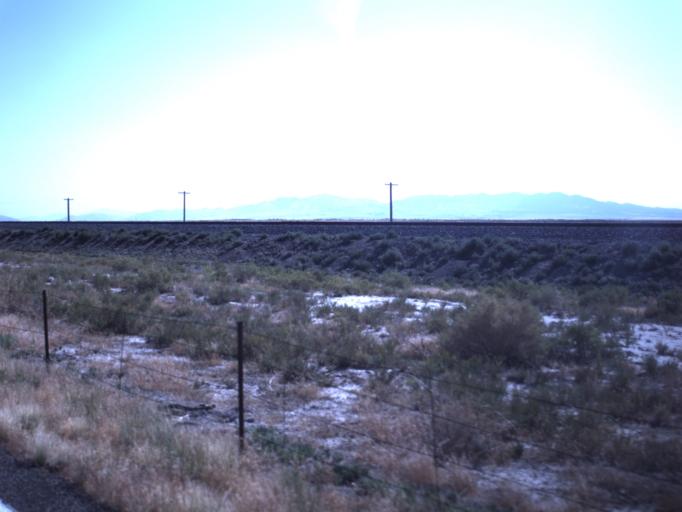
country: US
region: Utah
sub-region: Millard County
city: Delta
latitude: 39.1995
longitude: -112.6884
